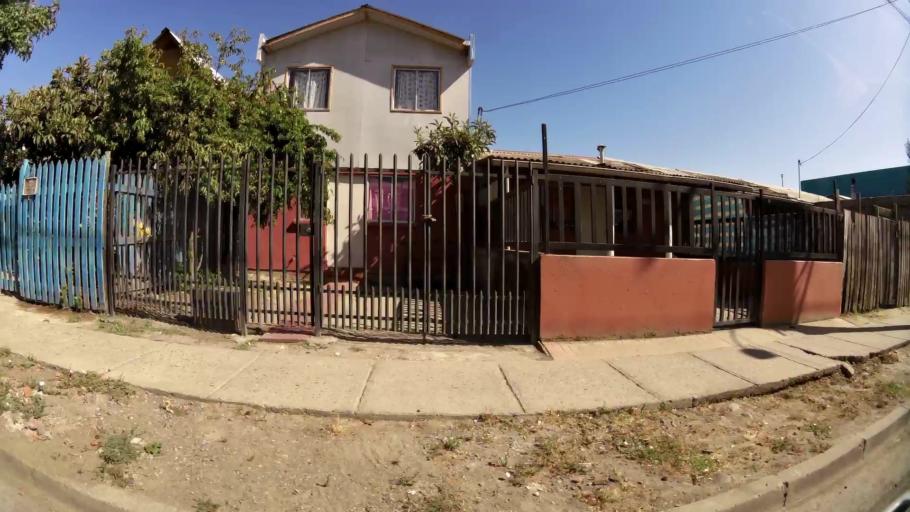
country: CL
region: Maule
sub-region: Provincia de Talca
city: Talca
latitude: -35.4050
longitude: -71.6484
